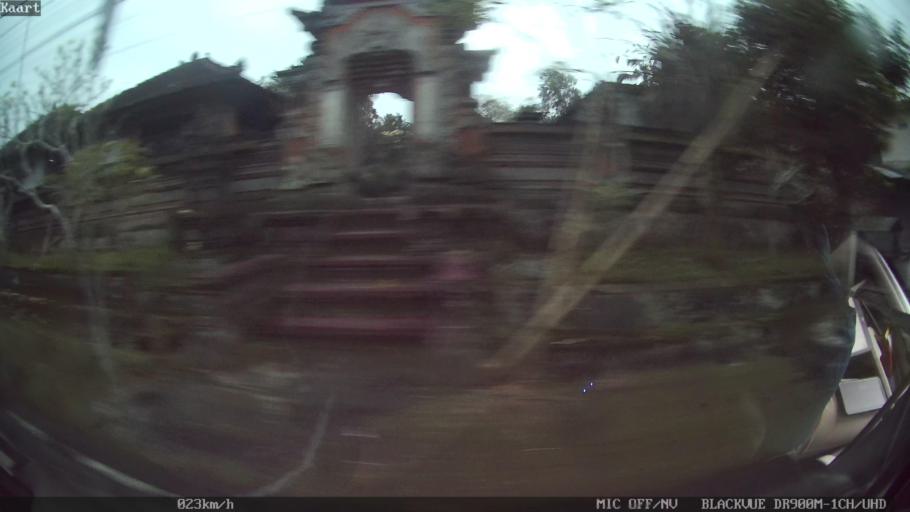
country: ID
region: Bali
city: Banjar Ponggang
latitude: -8.3890
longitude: 115.2607
